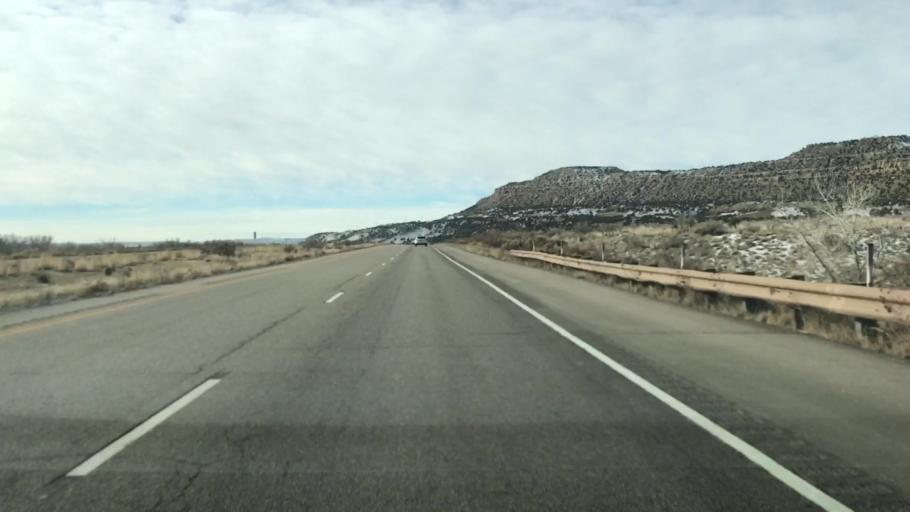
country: US
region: Colorado
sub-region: Garfield County
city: Parachute
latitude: 39.3491
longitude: -108.1840
